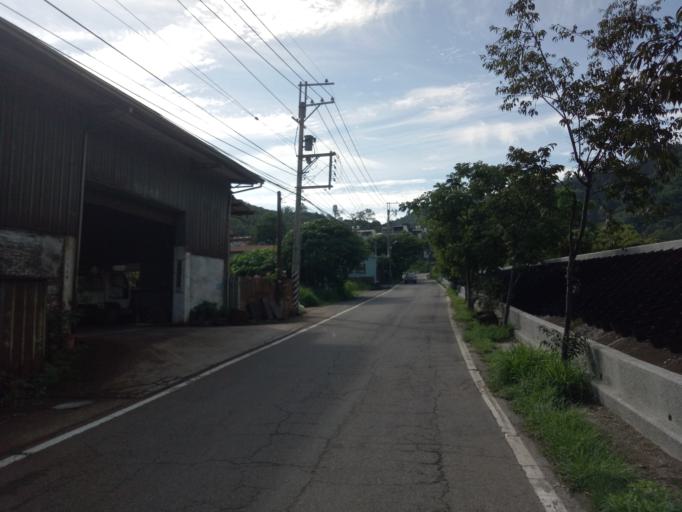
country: TW
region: Taiwan
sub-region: Taichung City
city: Taichung
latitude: 24.0866
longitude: 120.7353
